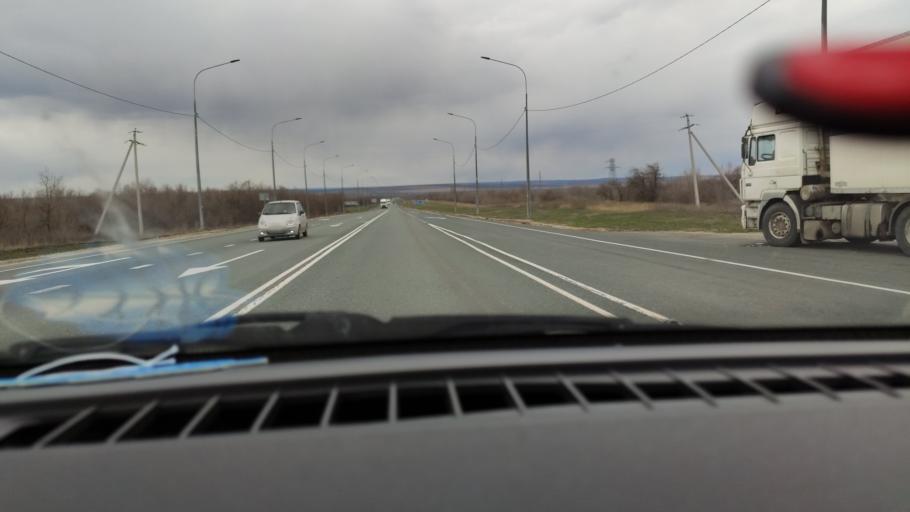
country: RU
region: Saratov
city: Yelshanka
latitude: 51.8259
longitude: 46.2835
